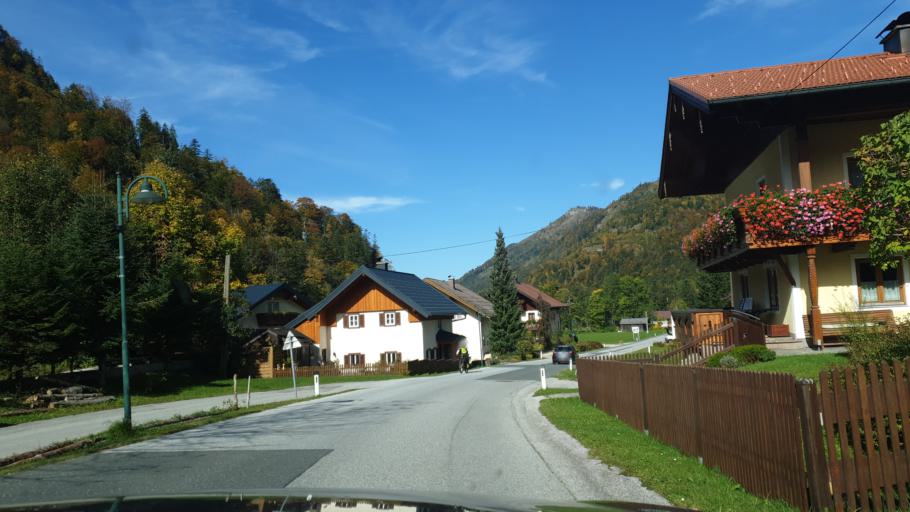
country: AT
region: Salzburg
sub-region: Politischer Bezirk Salzburg-Umgebung
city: Hintersee
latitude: 47.7150
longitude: 13.2858
